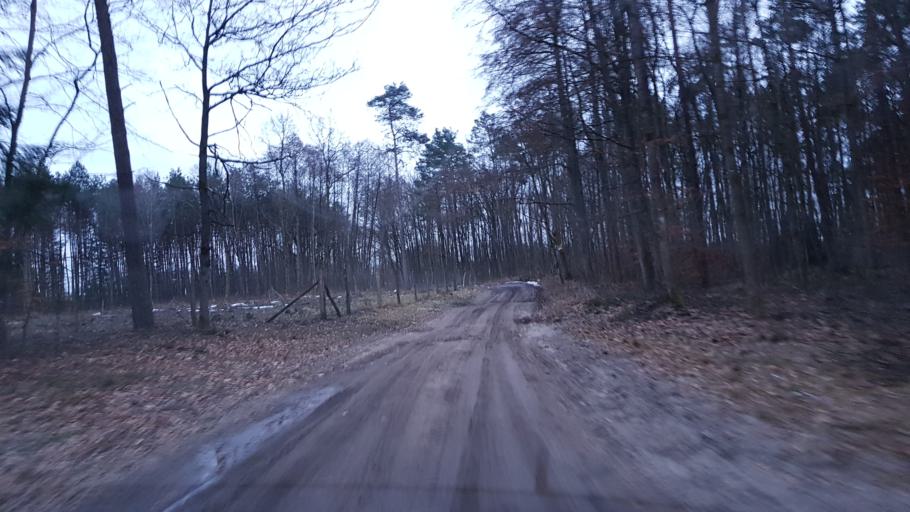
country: PL
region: Greater Poland Voivodeship
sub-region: Powiat zlotowski
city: Sypniewo
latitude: 53.4885
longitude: 16.6887
